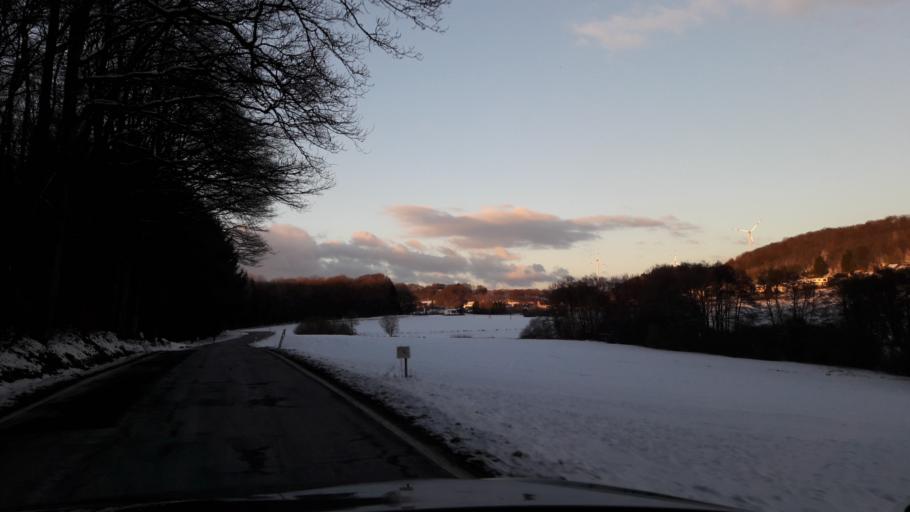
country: DE
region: Rheinland-Pfalz
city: Gimbweiler
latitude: 49.5769
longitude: 7.1848
